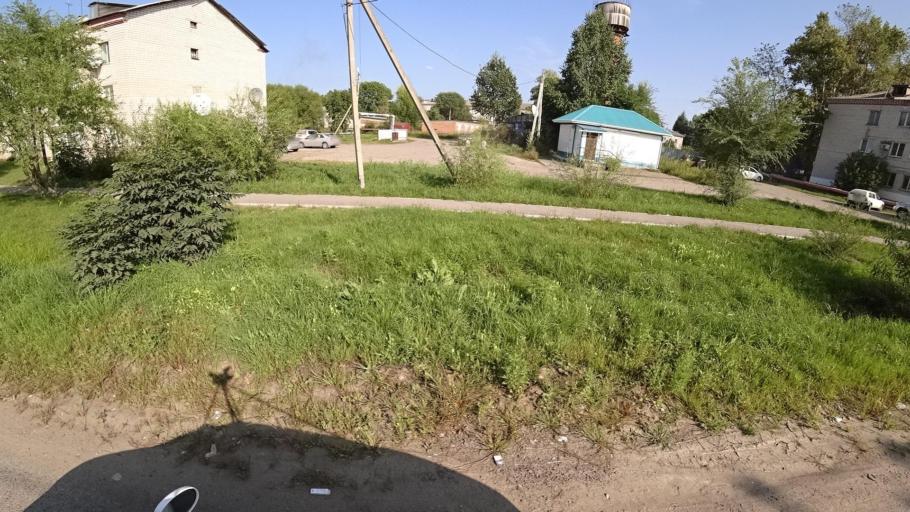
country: RU
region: Khabarovsk Krai
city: Khor
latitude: 47.9707
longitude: 135.0522
